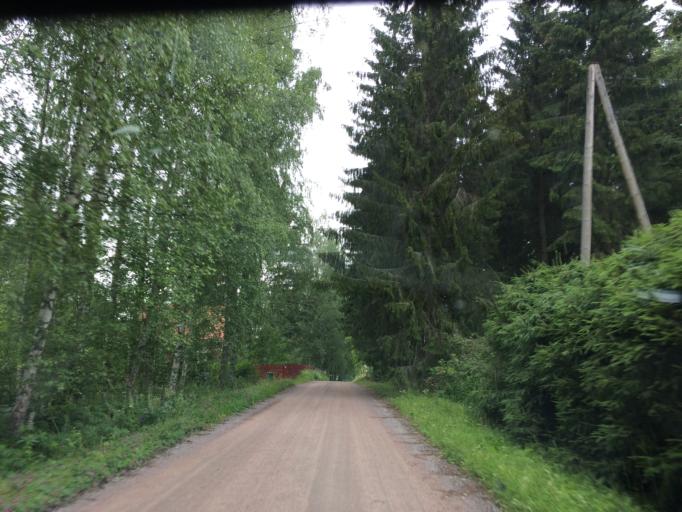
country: FI
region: Haeme
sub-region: Haemeenlinna
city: Janakkala
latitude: 60.8465
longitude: 24.5242
